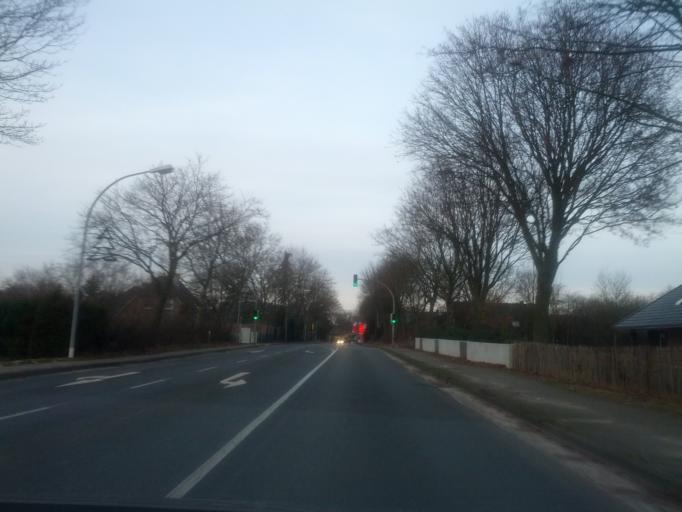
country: DE
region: Lower Saxony
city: Hollenstedt
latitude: 53.3628
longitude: 9.7113
